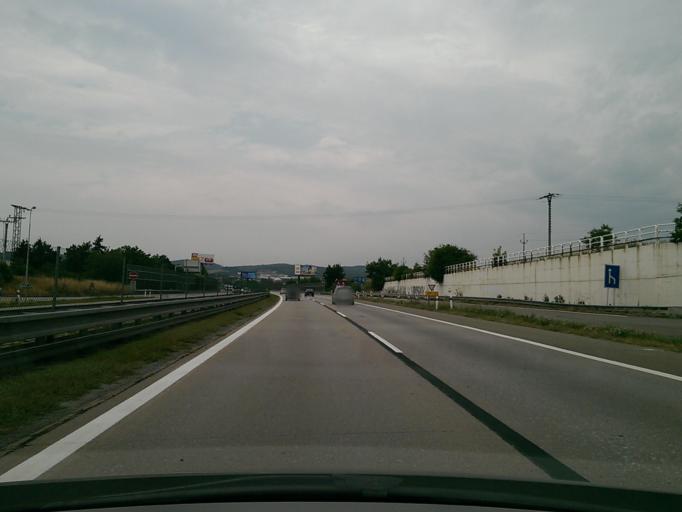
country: CZ
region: South Moravian
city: Troubsko
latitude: 49.1739
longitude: 16.5123
